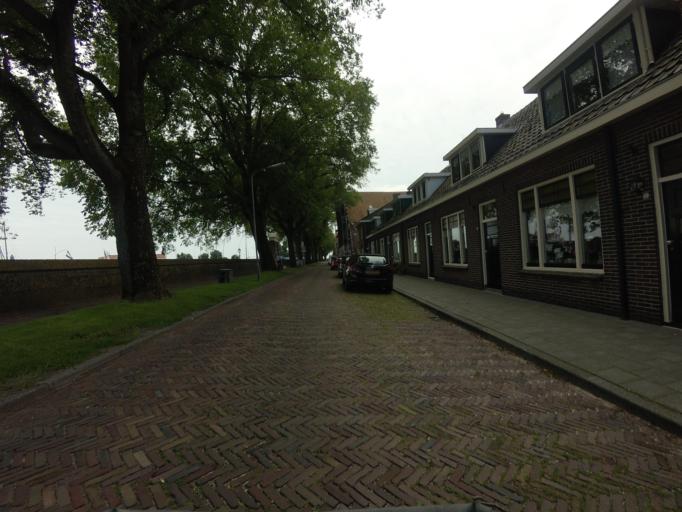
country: NL
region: North Holland
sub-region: Gemeente Enkhuizen
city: Enkhuizen
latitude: 52.7043
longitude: 5.2975
